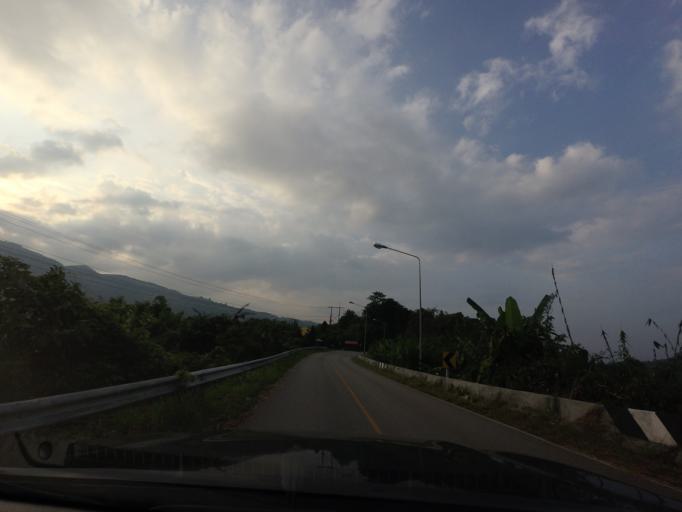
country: TH
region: Loei
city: Na Haeo
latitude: 17.3692
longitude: 101.0495
